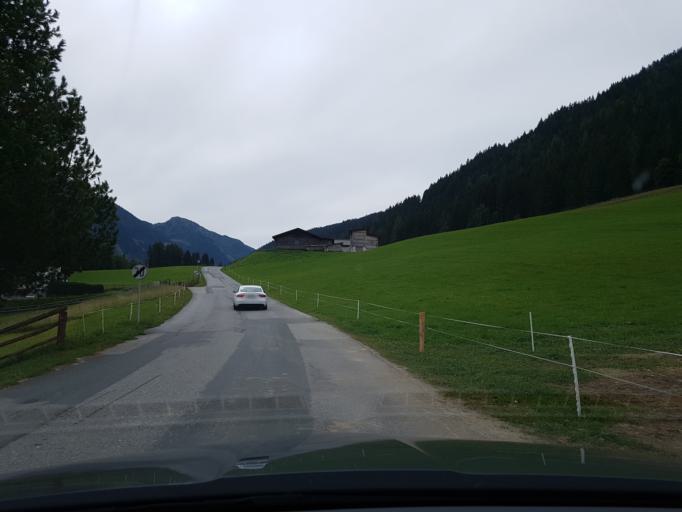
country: AT
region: Salzburg
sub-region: Politischer Bezirk Sankt Johann im Pongau
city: Forstau
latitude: 47.3741
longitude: 13.5500
